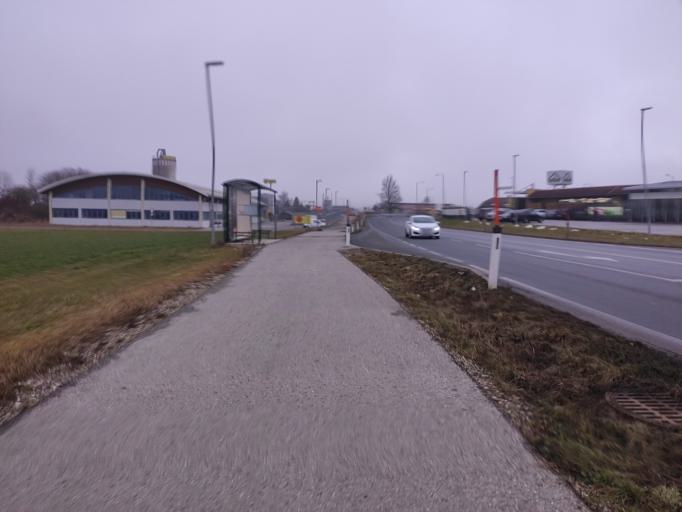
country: AT
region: Salzburg
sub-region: Politischer Bezirk Salzburg-Umgebung
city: Neumarkt am Wallersee
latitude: 47.9571
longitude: 13.2343
